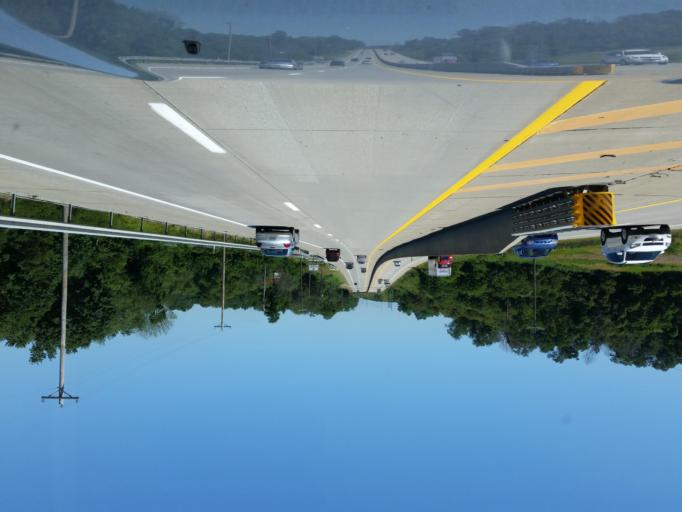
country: US
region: Pennsylvania
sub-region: Westmoreland County
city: Loyalhanna
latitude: 40.4159
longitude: -79.3737
